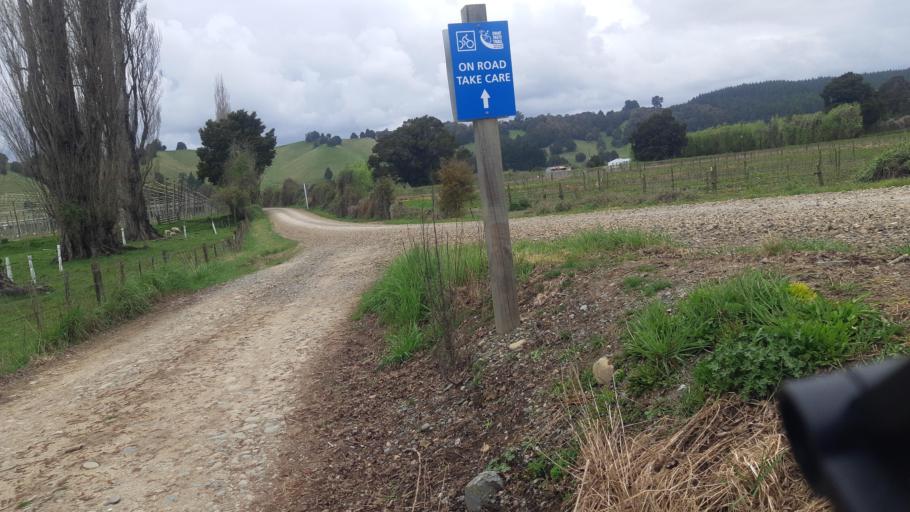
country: NZ
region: Tasman
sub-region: Tasman District
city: Wakefield
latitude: -41.4165
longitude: 173.0040
